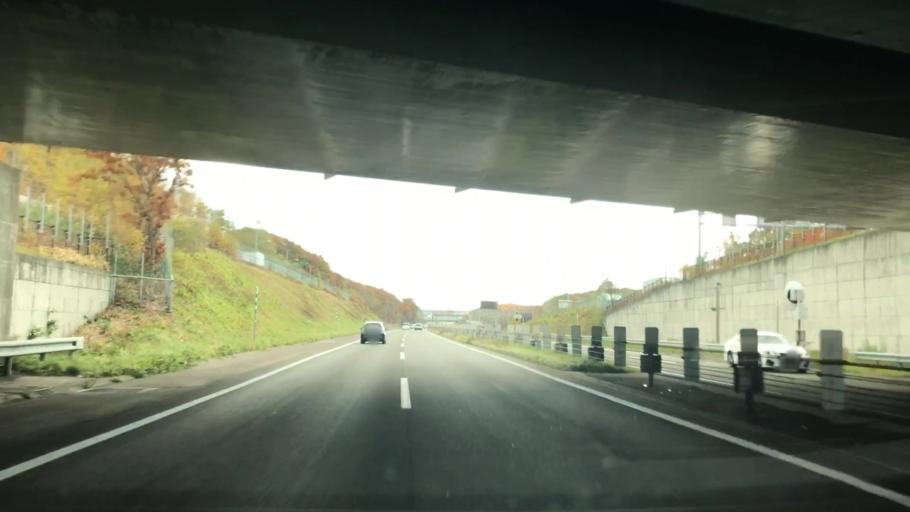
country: JP
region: Hokkaido
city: Kitahiroshima
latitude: 43.0094
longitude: 141.4662
